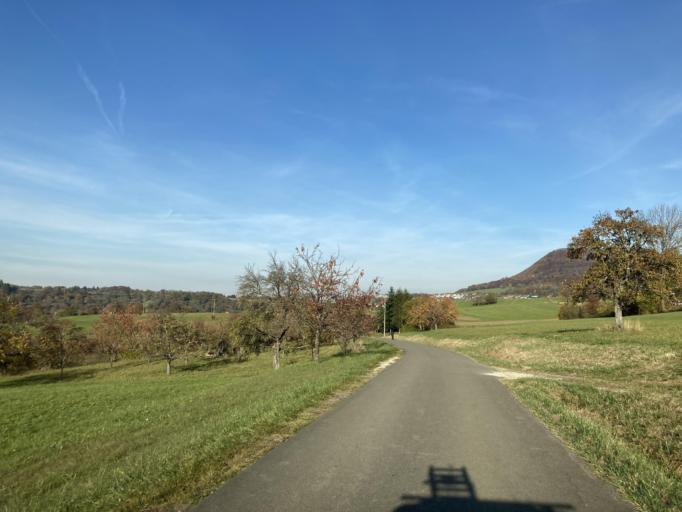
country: DE
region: Baden-Wuerttemberg
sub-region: Tuebingen Region
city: Nehren
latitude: 48.4061
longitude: 9.0988
